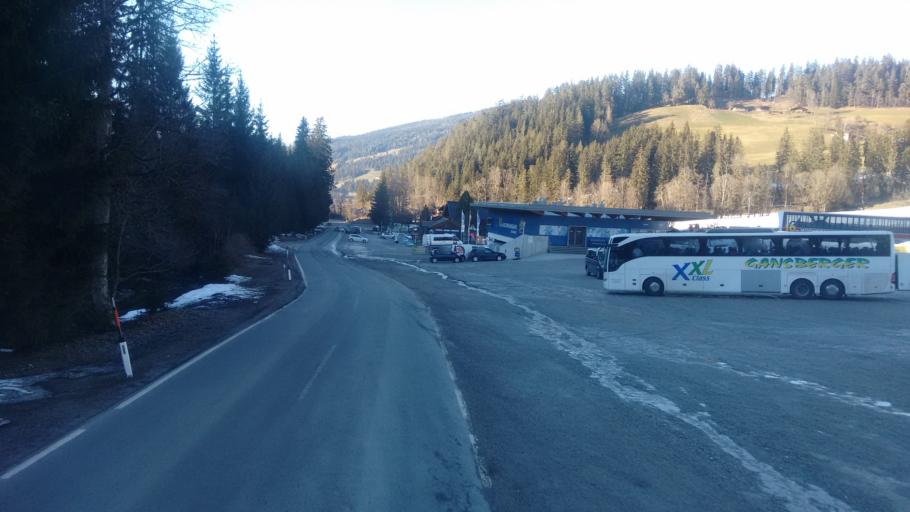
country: AT
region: Salzburg
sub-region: Politischer Bezirk Sankt Johann im Pongau
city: Altenmarkt im Pongau
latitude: 47.3605
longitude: 13.4265
